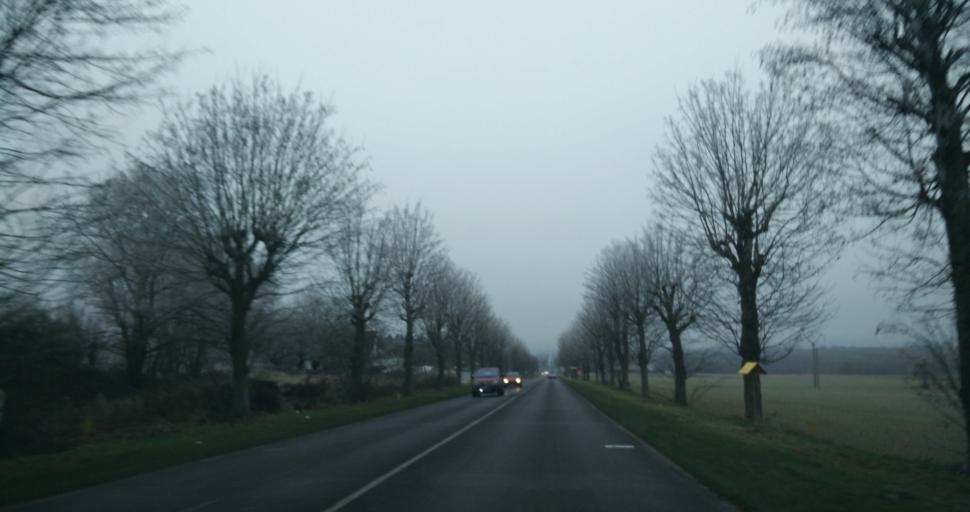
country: FR
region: Haute-Normandie
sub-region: Departement de l'Eure
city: Courcelles-sur-Seine
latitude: 49.1490
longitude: 1.3860
